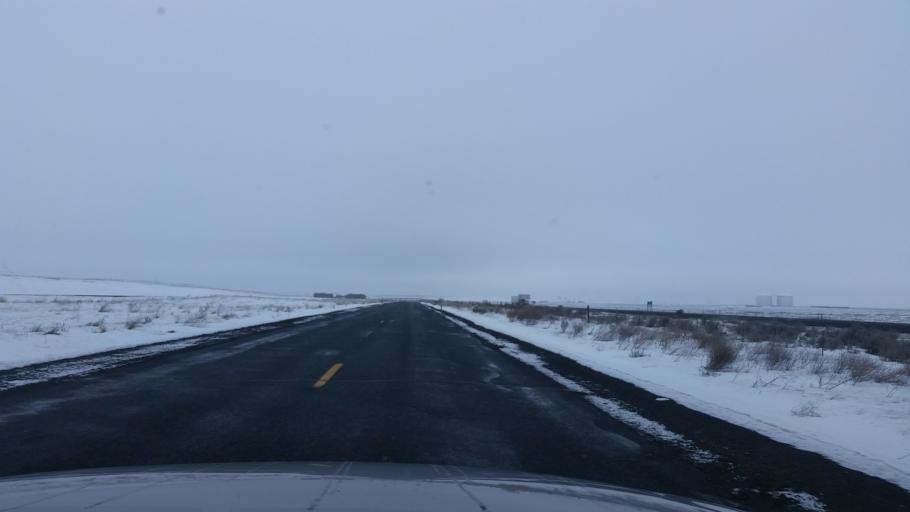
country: US
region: Washington
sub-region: Adams County
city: Ritzville
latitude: 47.2180
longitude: -118.2020
